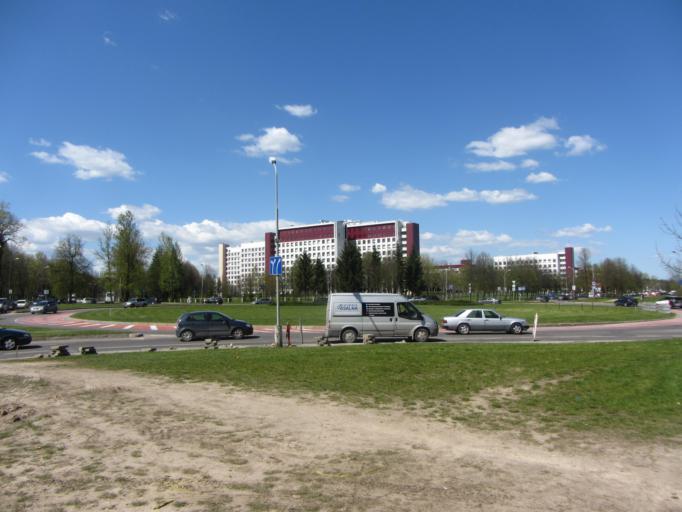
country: LT
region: Vilnius County
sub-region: Vilnius
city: Fabijoniskes
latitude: 54.7491
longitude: 25.2798
